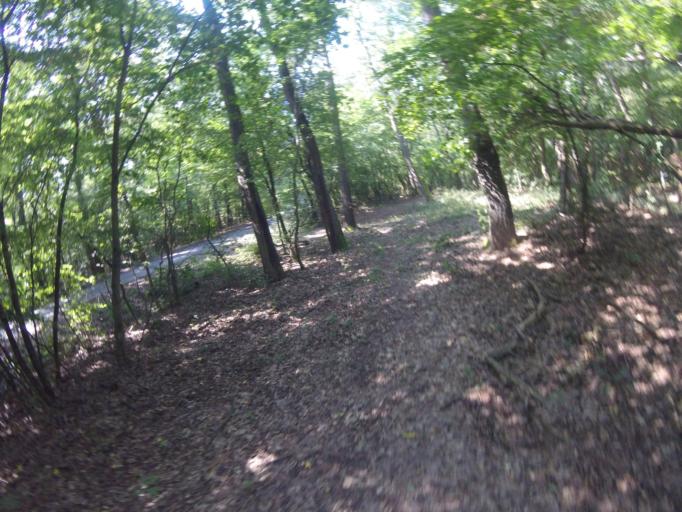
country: HU
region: Nograd
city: Bujak
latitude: 47.8959
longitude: 19.5267
